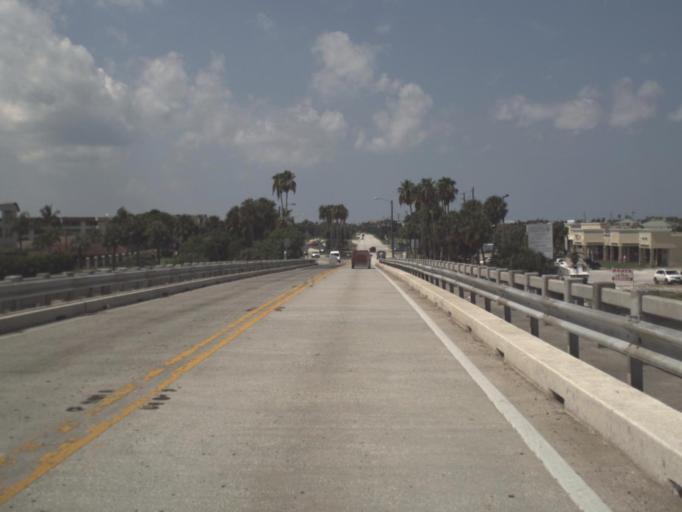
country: US
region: Florida
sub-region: Pinellas County
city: Tierra Verde
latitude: 27.6929
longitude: -82.7184
